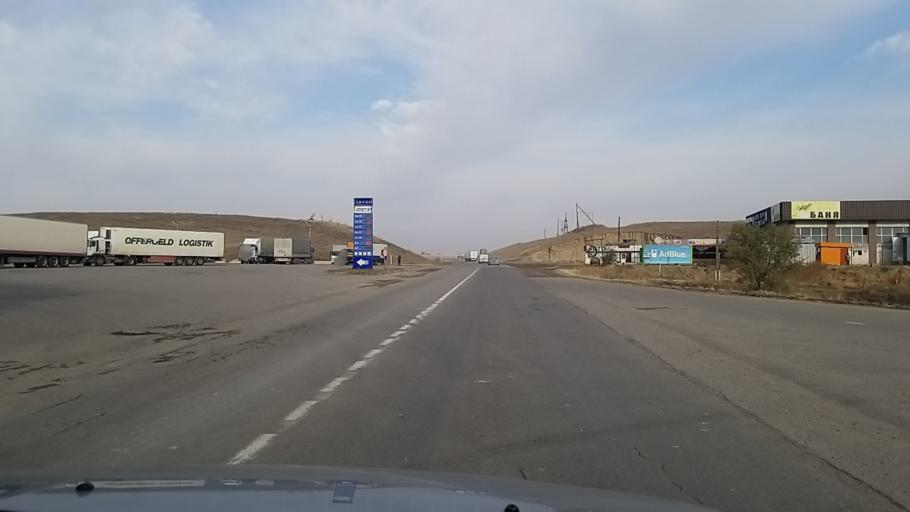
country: KZ
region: Almaty Oblysy
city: Burunday
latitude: 43.4638
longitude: 76.7079
